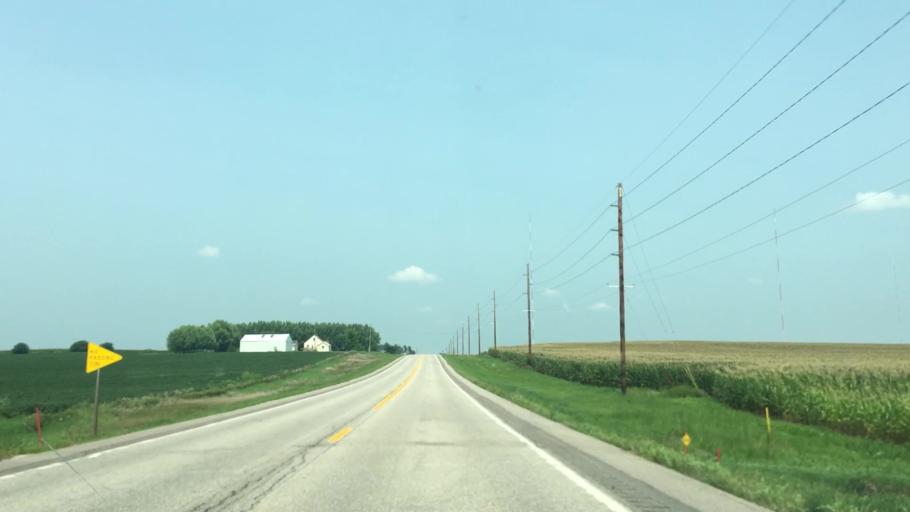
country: US
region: Iowa
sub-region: Benton County
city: Urbana
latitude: 42.2728
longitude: -91.8904
